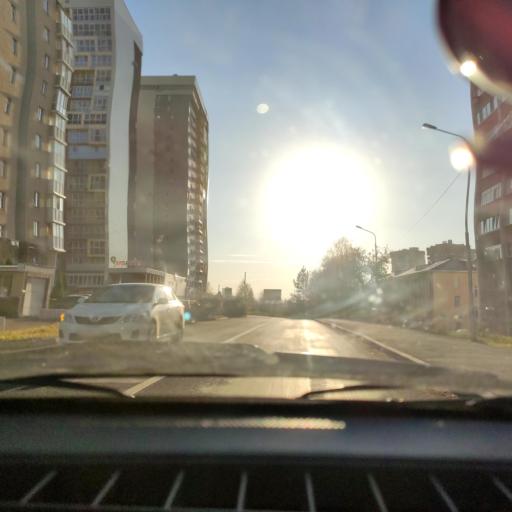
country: RU
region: Bashkortostan
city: Ufa
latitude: 54.7185
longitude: 55.9956
